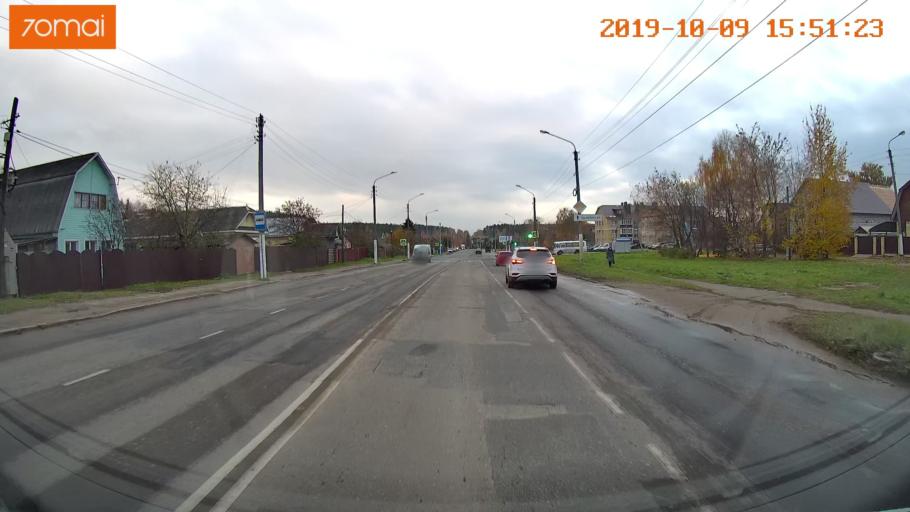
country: RU
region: Kostroma
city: Oktyabr'skiy
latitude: 57.7978
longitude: 40.9797
